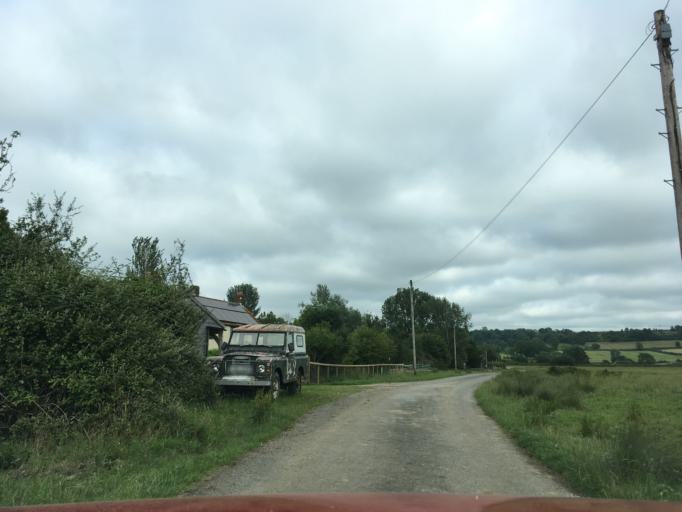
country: GB
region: England
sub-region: South Gloucestershire
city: Horton
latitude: 51.5829
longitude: -2.3520
